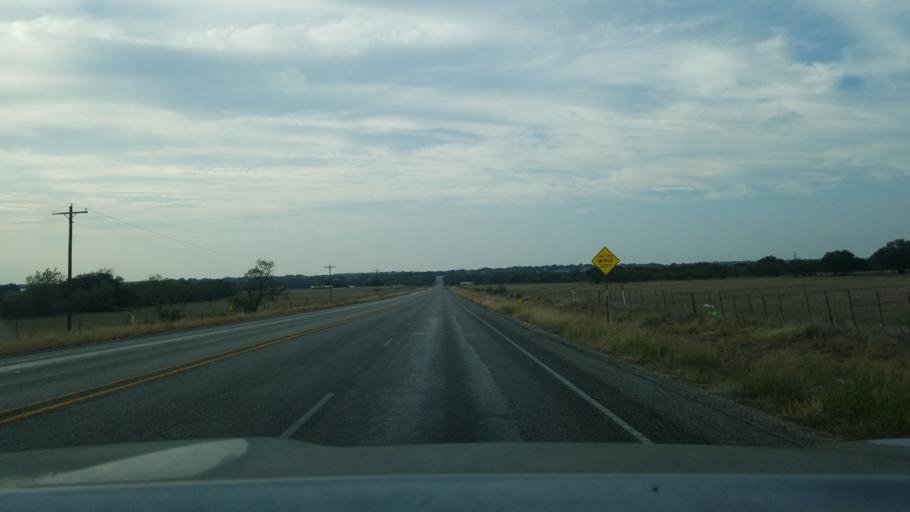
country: US
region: Texas
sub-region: Mills County
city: Goldthwaite
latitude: 31.5473
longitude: -98.6365
